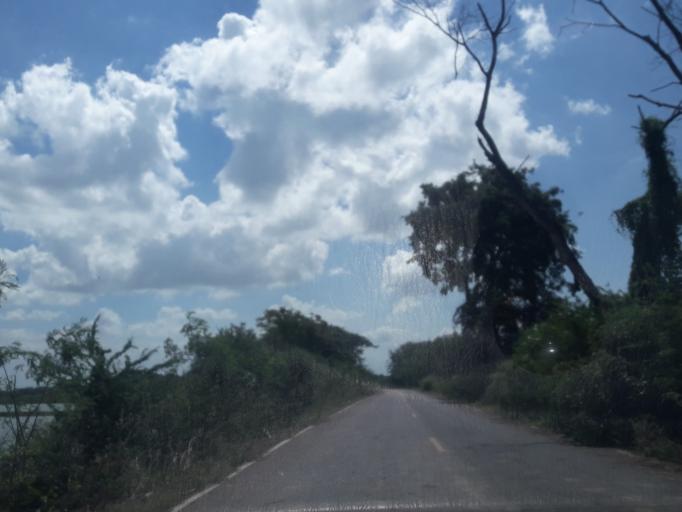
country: TH
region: Lop Buri
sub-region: Amphoe Tha Luang
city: Tha Luang
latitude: 15.0632
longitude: 101.0320
